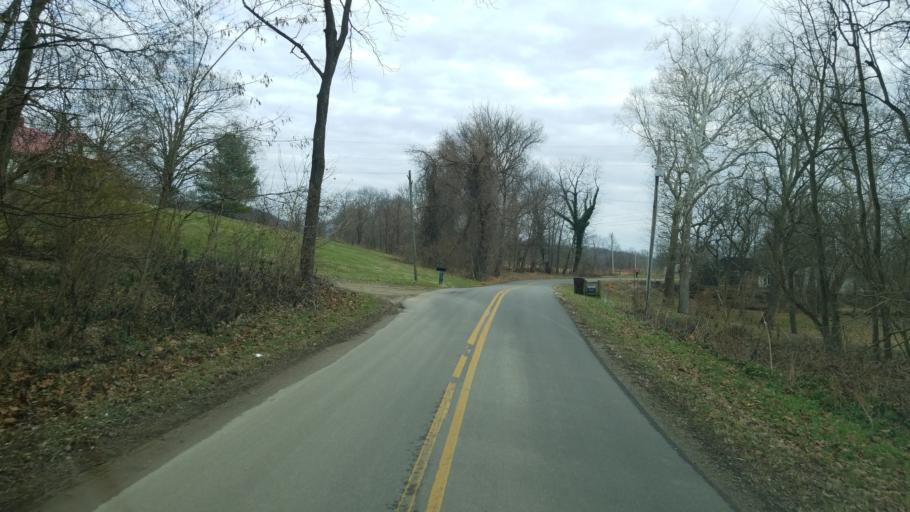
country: US
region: Ohio
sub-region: Highland County
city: Greenfield
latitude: 39.2356
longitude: -83.3363
